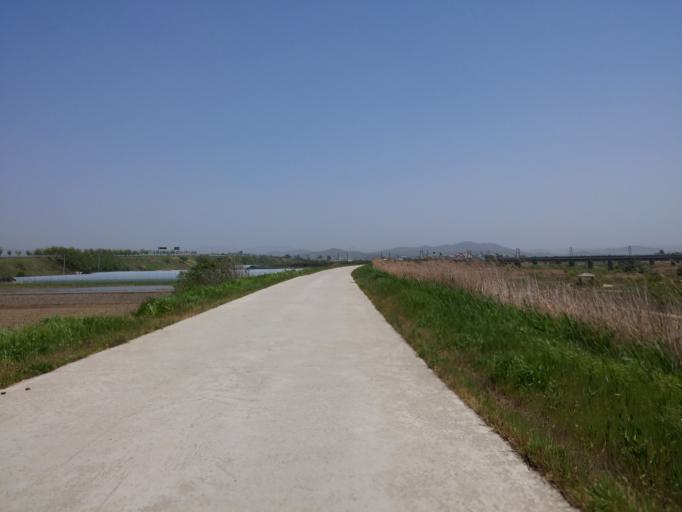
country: KR
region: Chungcheongnam-do
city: Nonsan
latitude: 36.2157
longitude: 127.1070
